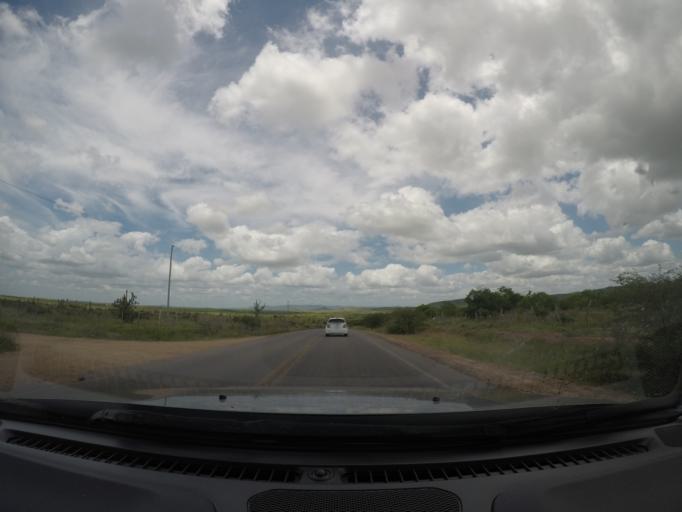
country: BR
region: Bahia
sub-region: Ipira
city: Ipira
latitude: -12.2759
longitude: -39.8530
